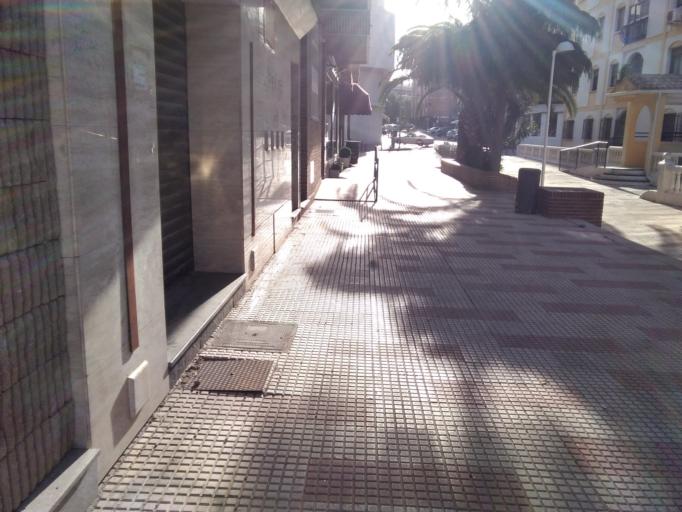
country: ES
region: Castille-La Mancha
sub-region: Province of Toledo
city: Toledo
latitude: 39.8681
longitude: -4.0332
